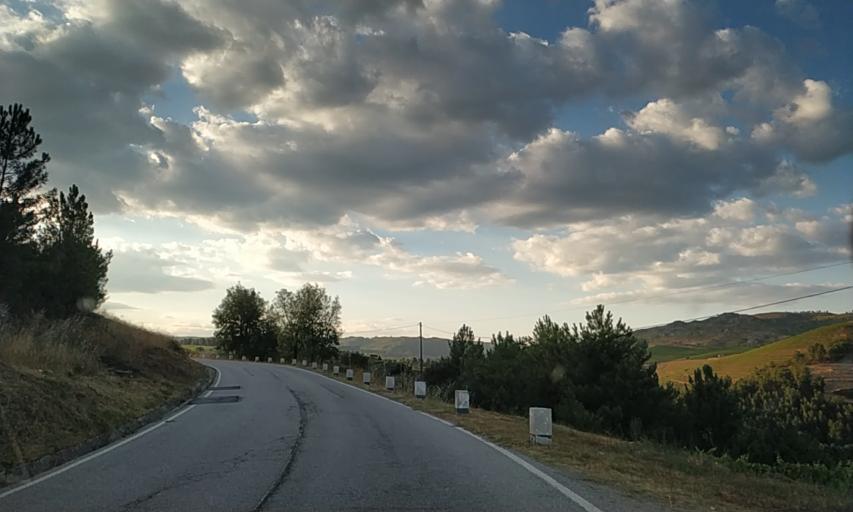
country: PT
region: Vila Real
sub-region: Sabrosa
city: Sabrosa
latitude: 41.2661
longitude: -7.4505
